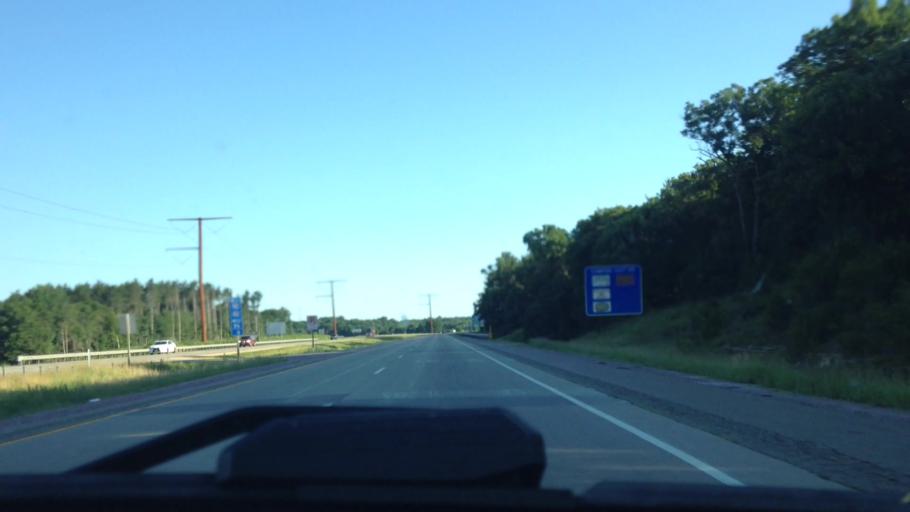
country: US
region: Wisconsin
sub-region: Columbia County
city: Wisconsin Dells
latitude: 43.6394
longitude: -89.8105
